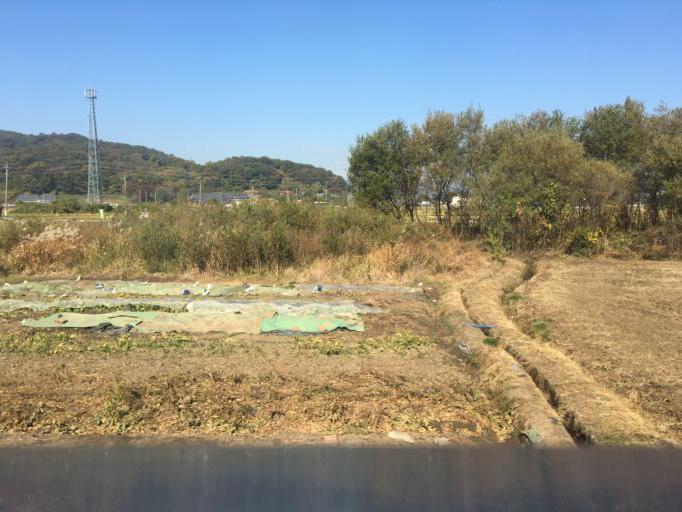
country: JP
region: Tochigi
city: Sano
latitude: 36.3255
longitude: 139.6293
